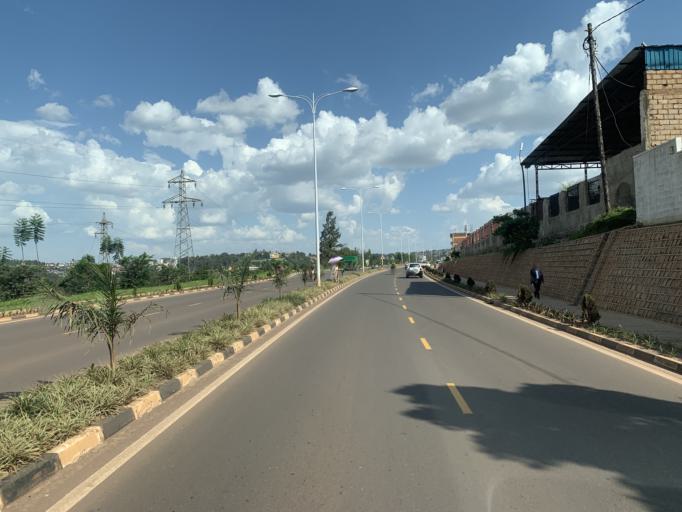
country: RW
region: Kigali
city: Kigali
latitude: -1.9645
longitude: 30.0797
